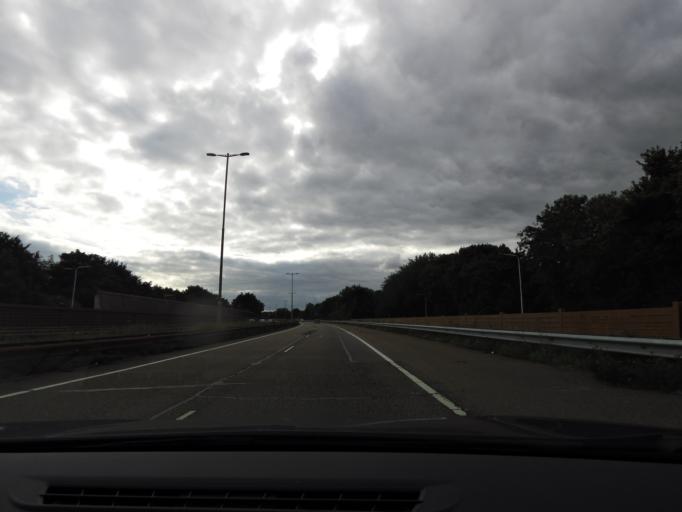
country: NL
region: Utrecht
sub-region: Gemeente Utrecht
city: Lunetten
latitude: 52.0680
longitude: 5.1286
